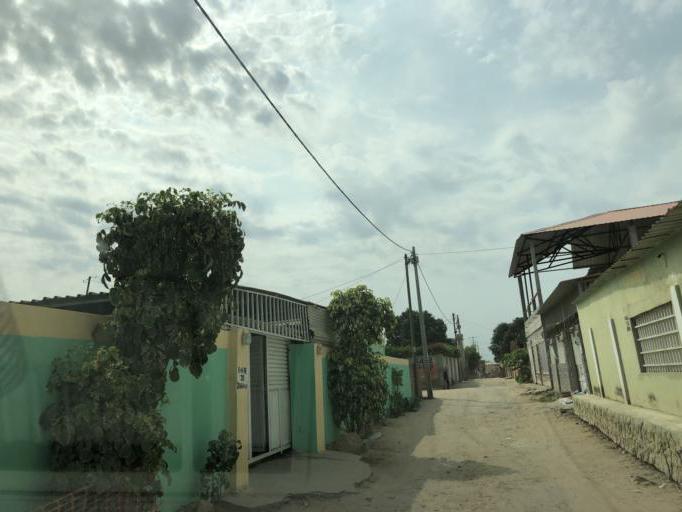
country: AO
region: Luanda
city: Luanda
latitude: -8.8974
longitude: 13.3533
